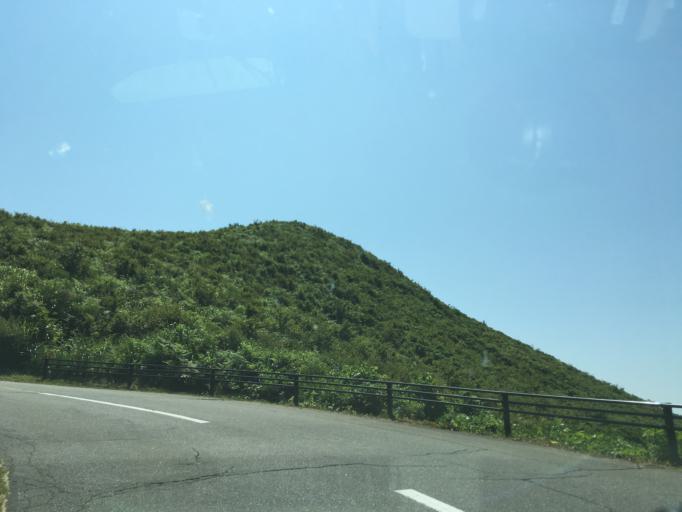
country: JP
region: Akita
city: Tenno
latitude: 39.9335
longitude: 139.8714
